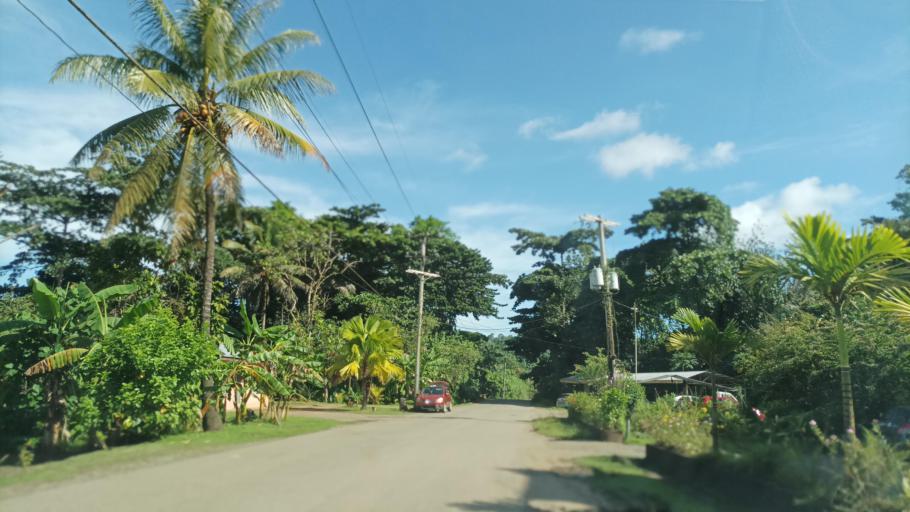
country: FM
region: Kosrae
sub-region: Lelu Municipality
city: Tofol
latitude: 5.3315
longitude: 163.0078
